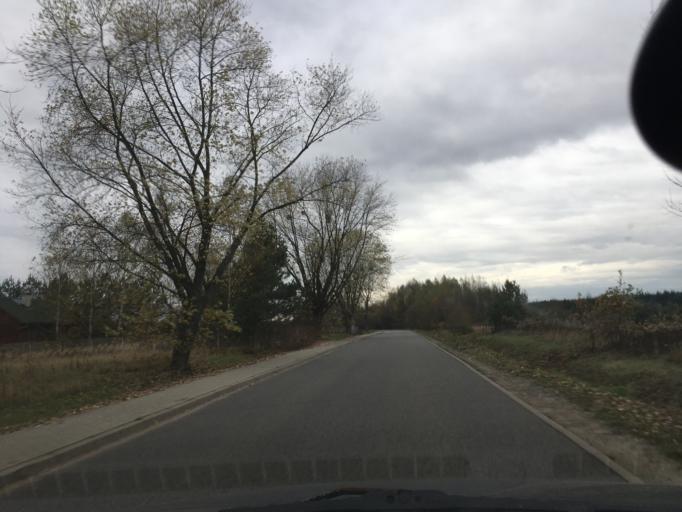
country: PL
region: Lodz Voivodeship
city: Zabia Wola
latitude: 52.0265
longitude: 20.7041
